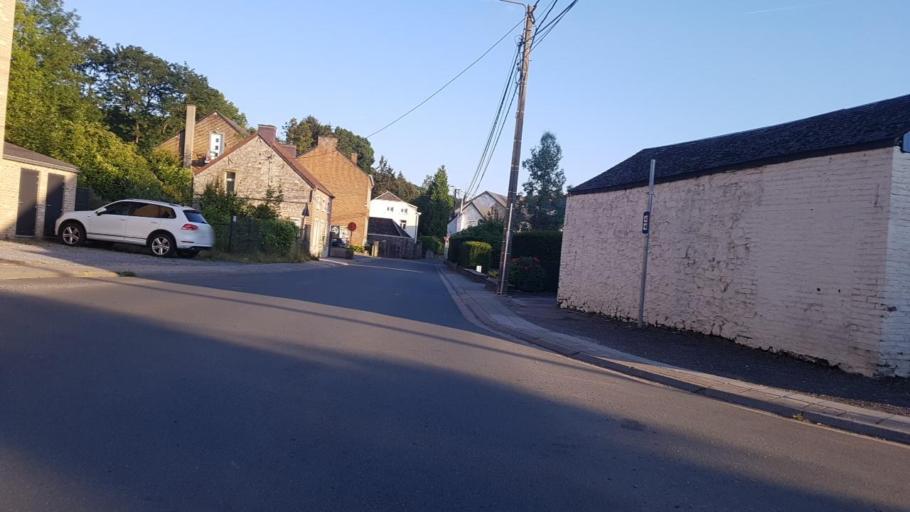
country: BE
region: Wallonia
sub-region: Province de Namur
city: Floreffe
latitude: 50.4425
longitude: 4.7944
